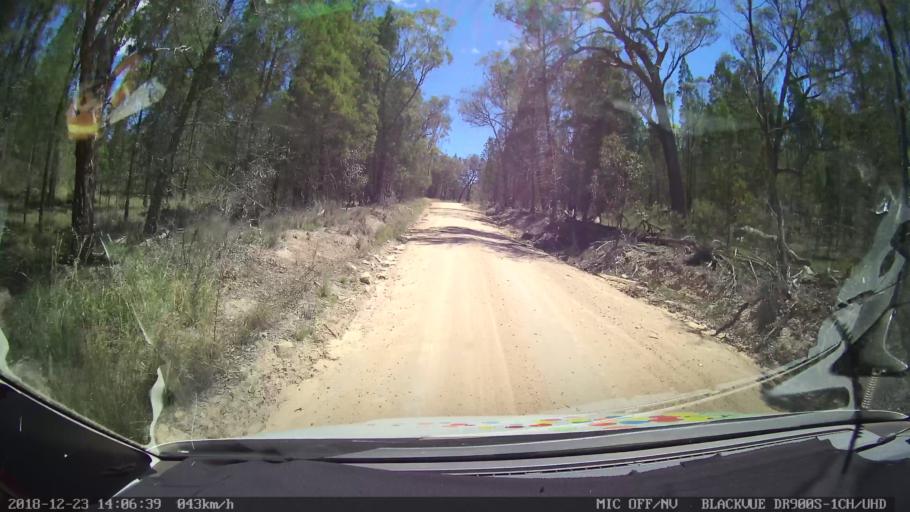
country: AU
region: New South Wales
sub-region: Tamworth Municipality
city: Manilla
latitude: -30.6313
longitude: 151.0749
